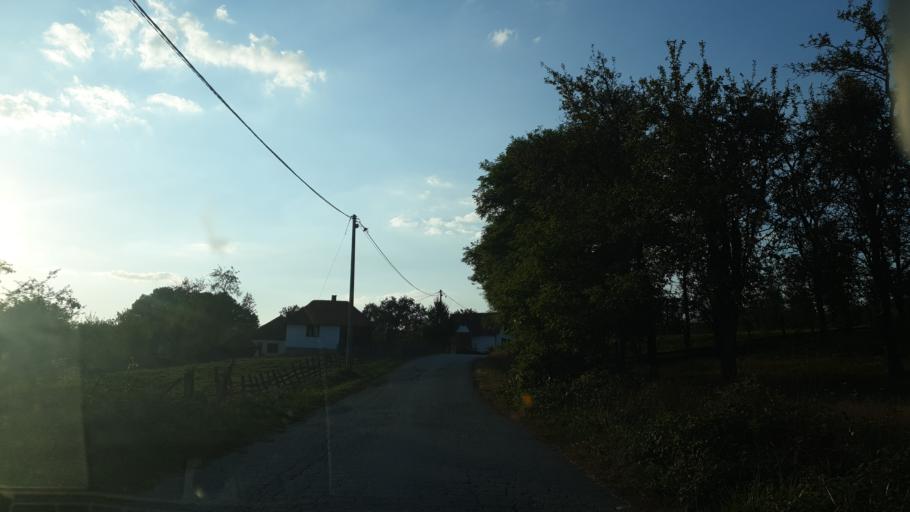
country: RS
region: Central Serbia
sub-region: Zlatiborski Okrug
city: Kosjeric
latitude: 43.9920
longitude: 20.0036
